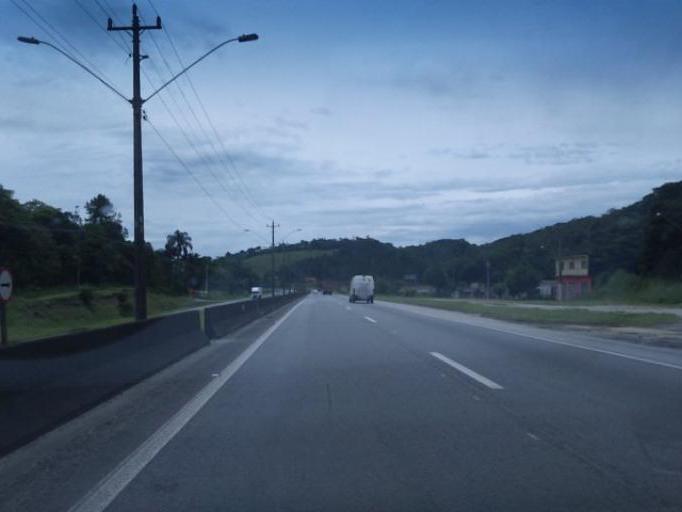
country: BR
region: Sao Paulo
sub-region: Sao Lourenco Da Serra
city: Sao Lourenco da Serra
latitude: -23.9056
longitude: -46.9918
